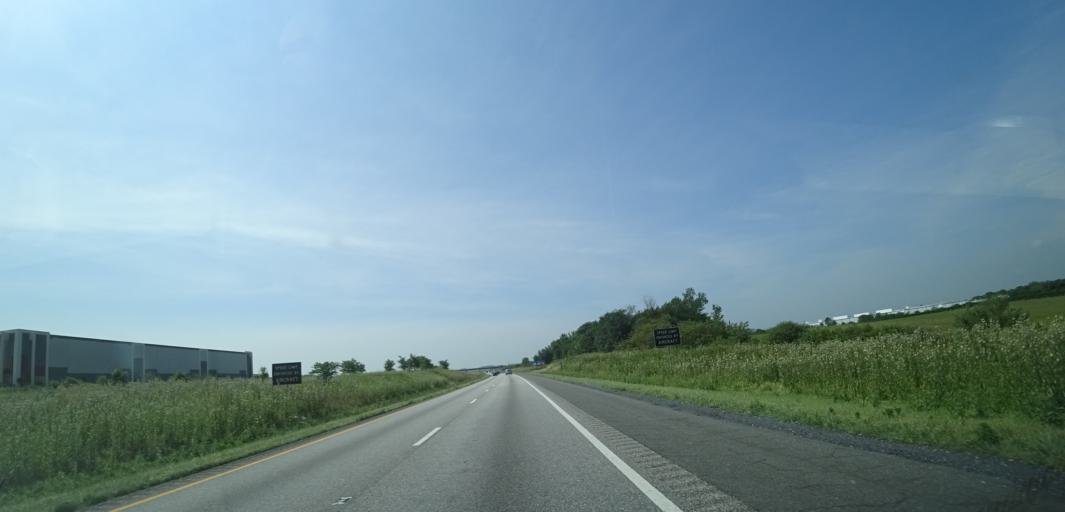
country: US
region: Virginia
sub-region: Rockingham County
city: Dayton
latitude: 38.3830
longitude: -78.9172
